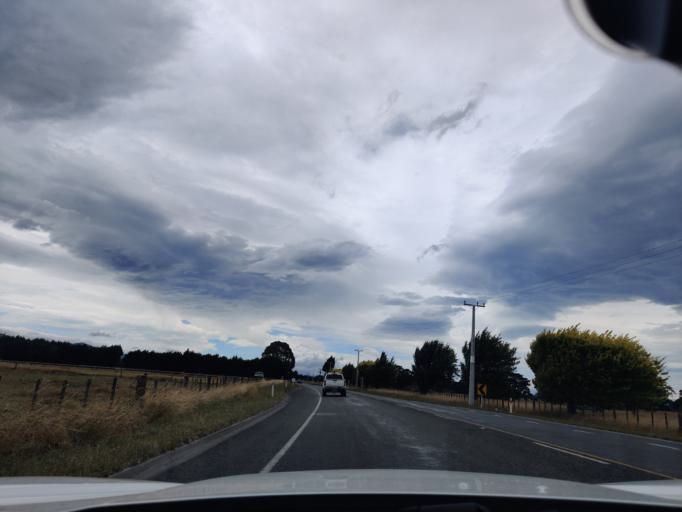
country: NZ
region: Wellington
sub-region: Masterton District
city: Masterton
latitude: -41.0050
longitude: 175.5557
